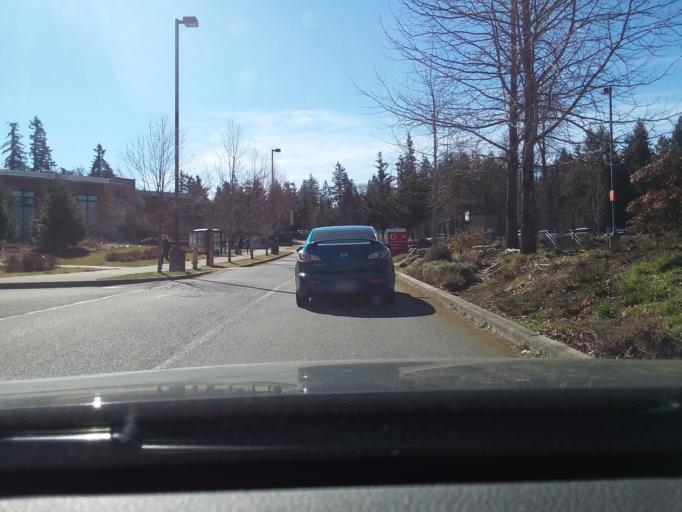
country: US
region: Washington
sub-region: Pierce County
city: South Hill
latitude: 47.1582
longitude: -122.2740
